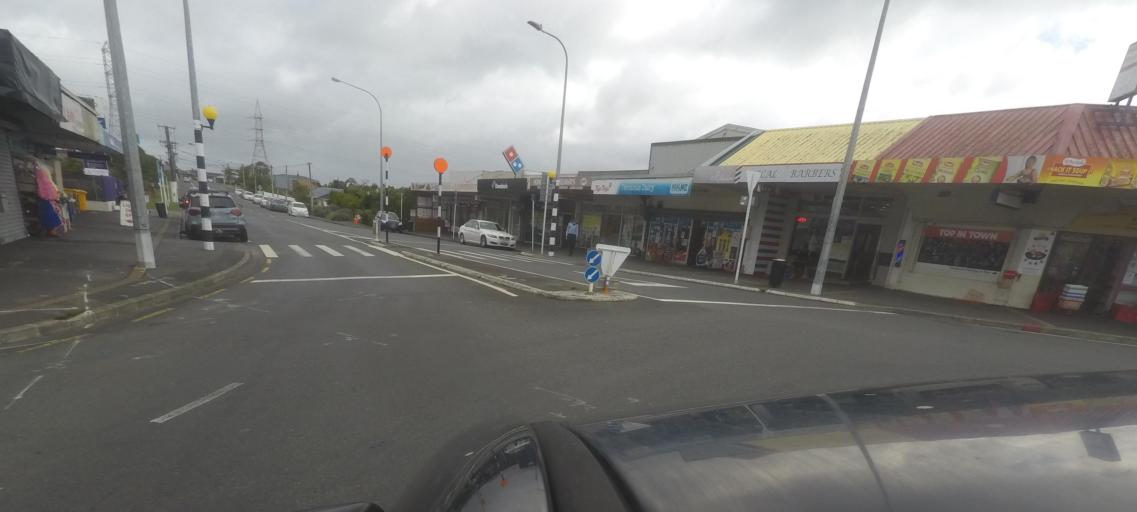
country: NZ
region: Auckland
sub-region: Auckland
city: Auckland
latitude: -36.9205
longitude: 174.7362
